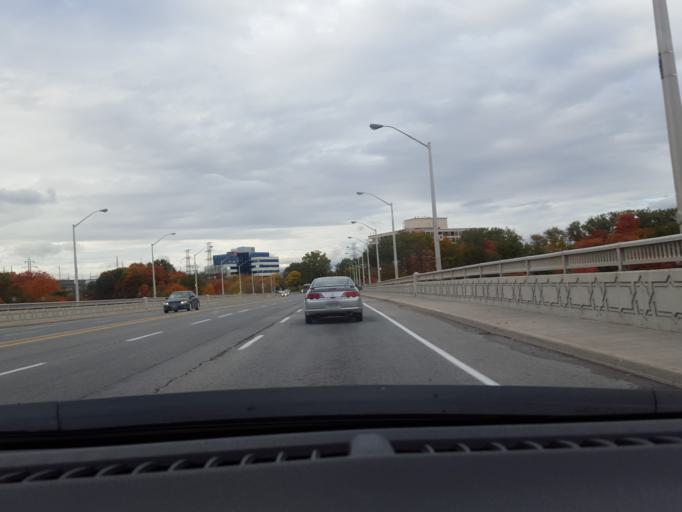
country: CA
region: Ontario
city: Toronto
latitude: 43.6989
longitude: -79.3502
